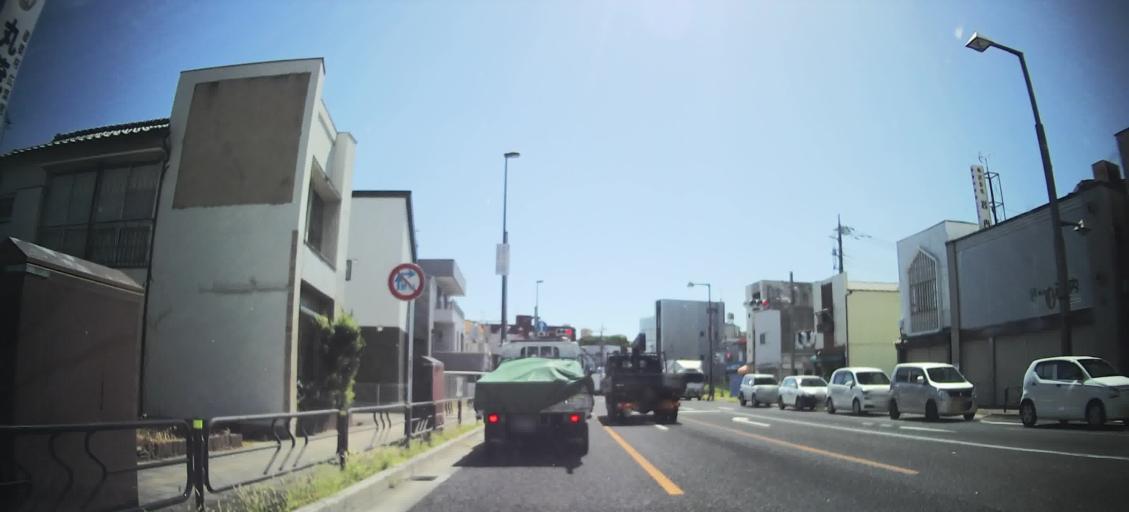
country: JP
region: Gunma
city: Maebashi-shi
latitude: 36.3883
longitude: 139.0735
